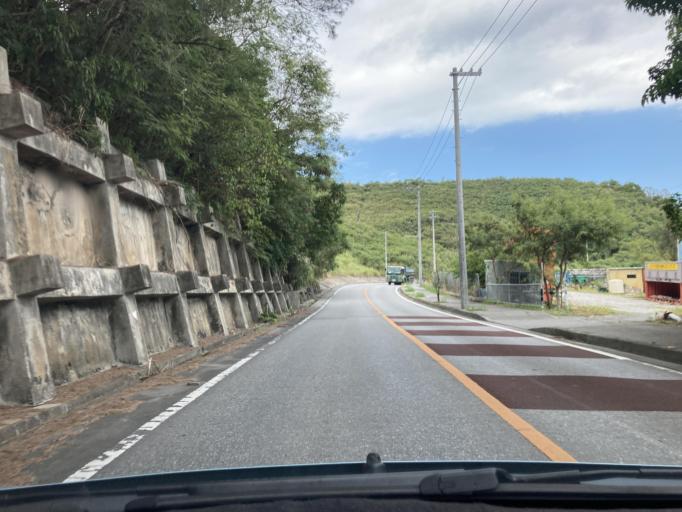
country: JP
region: Okinawa
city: Ginowan
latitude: 26.2620
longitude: 127.7837
